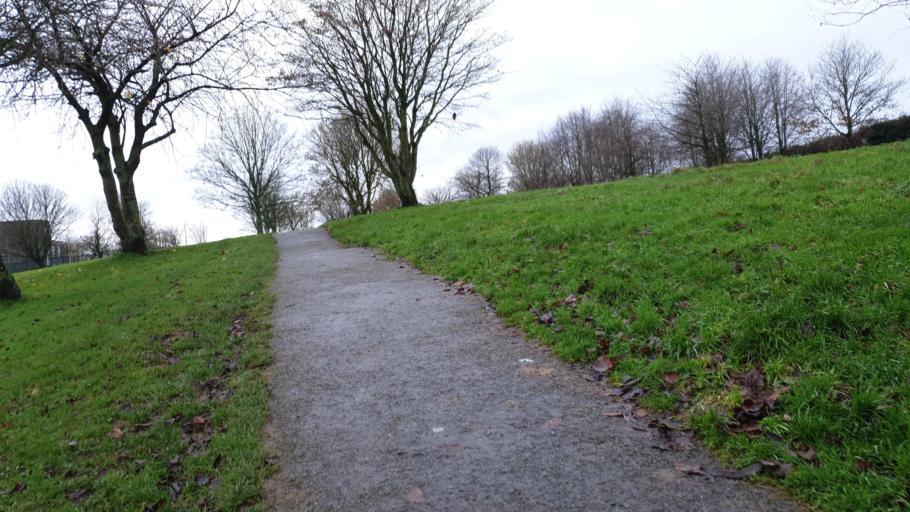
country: IE
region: Munster
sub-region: County Cork
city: Cork
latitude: 51.8908
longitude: -8.4295
